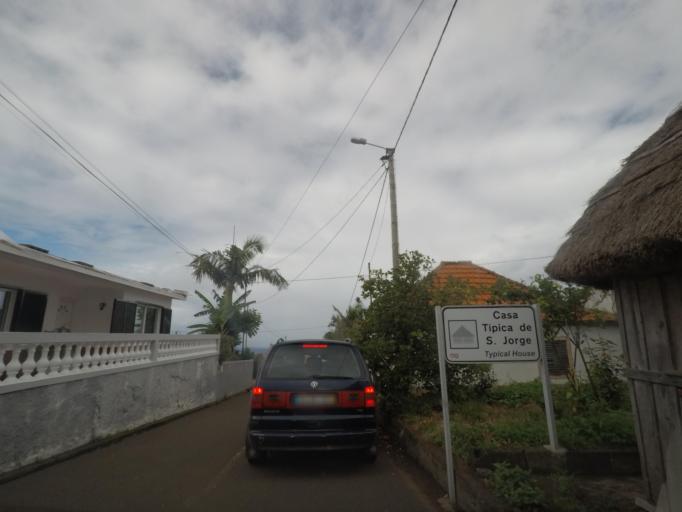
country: PT
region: Madeira
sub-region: Santana
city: Santana
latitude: 32.8328
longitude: -16.9078
